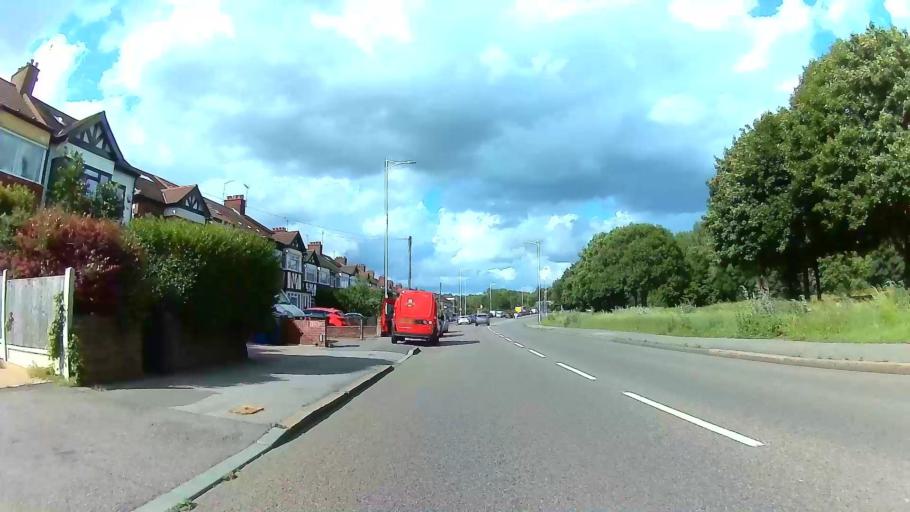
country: GB
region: England
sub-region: Greater London
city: Woodford Green
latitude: 51.6032
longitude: 0.0462
